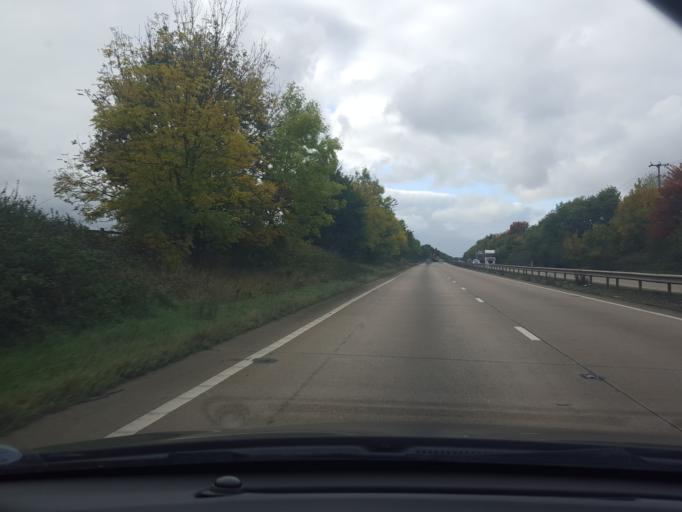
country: GB
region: England
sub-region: Suffolk
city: Elmswell
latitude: 52.2161
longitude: 0.9376
